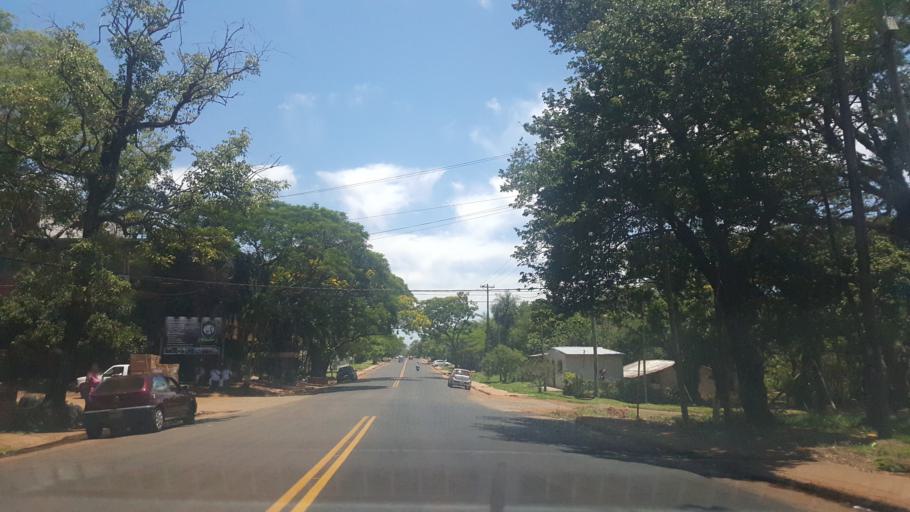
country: AR
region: Misiones
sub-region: Departamento de Capital
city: Posadas
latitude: -27.3610
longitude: -55.9266
